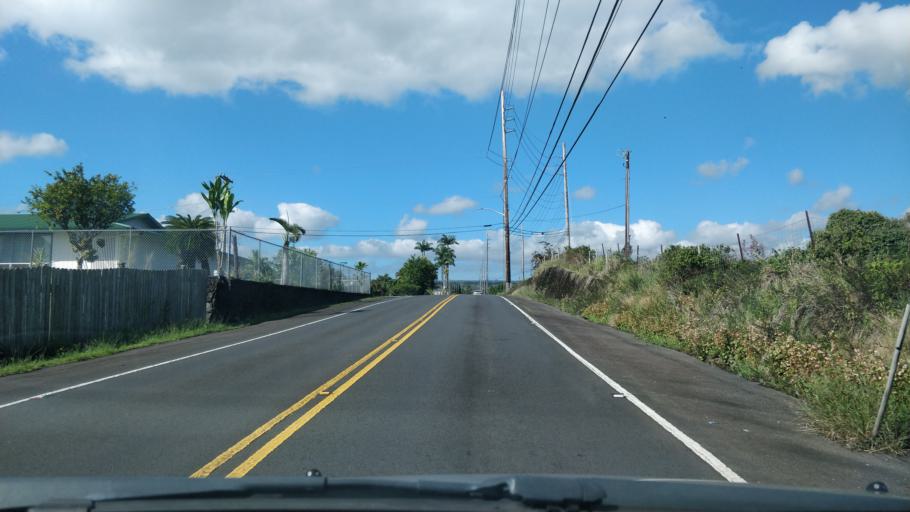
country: US
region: Hawaii
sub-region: Hawaii County
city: Hilo
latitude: 19.6827
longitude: -155.0959
